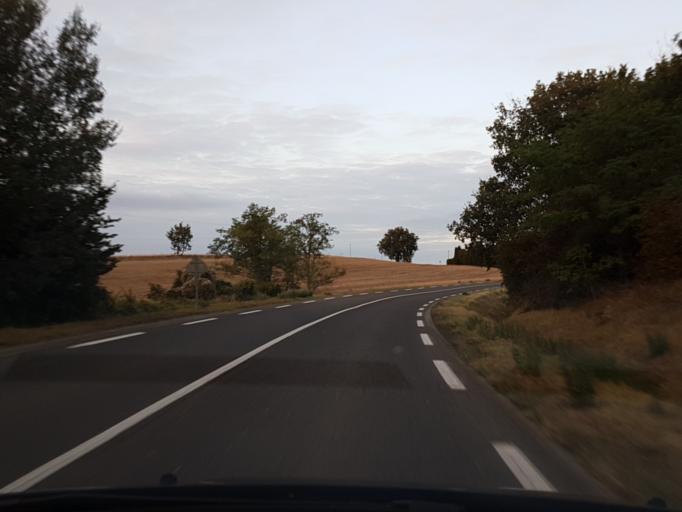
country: FR
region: Midi-Pyrenees
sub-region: Departement de l'Ariege
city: Mirepoix
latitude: 43.1455
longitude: 1.9552
